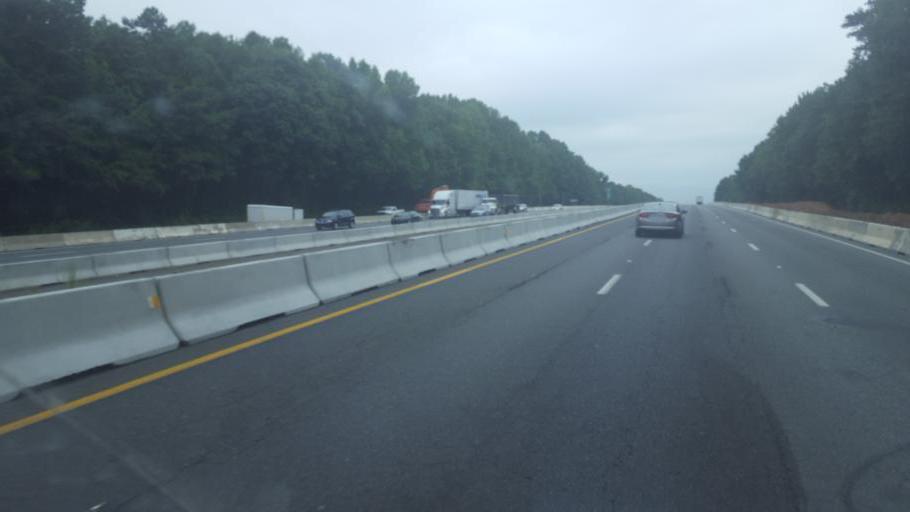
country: US
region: North Carolina
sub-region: Mecklenburg County
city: Huntersville
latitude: 35.3216
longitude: -80.8476
